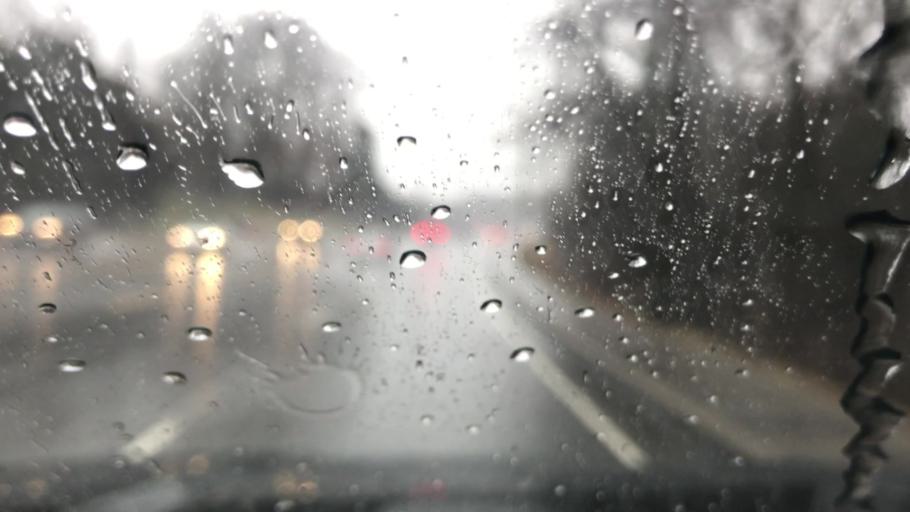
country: US
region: Tennessee
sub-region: Williamson County
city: Nolensville
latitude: 36.0469
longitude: -86.6802
